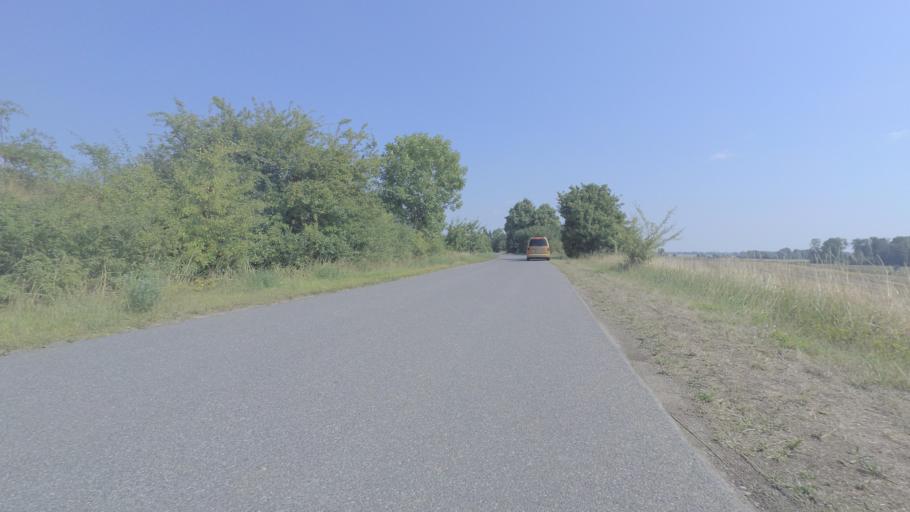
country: DE
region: Mecklenburg-Vorpommern
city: Pampow
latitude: 53.7260
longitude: 12.6594
